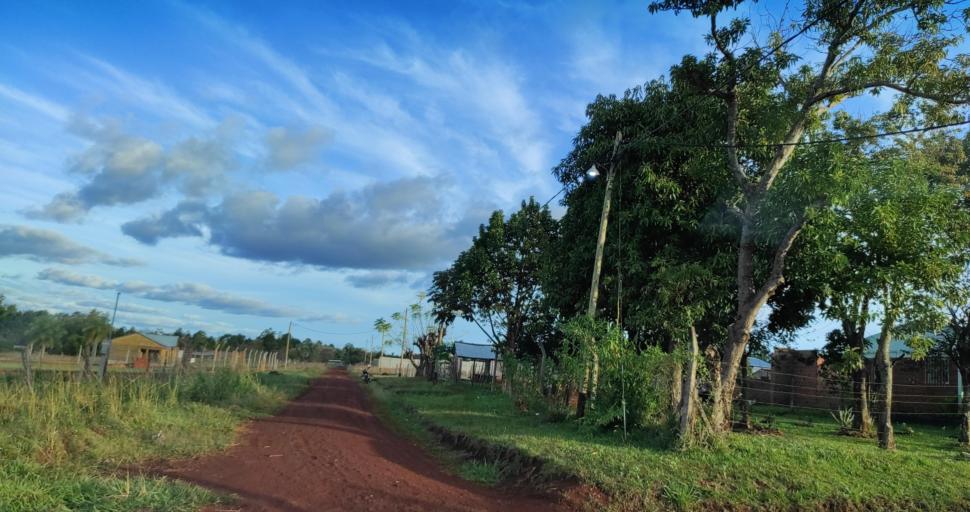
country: AR
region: Misiones
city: Garupa
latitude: -27.5229
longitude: -55.8536
